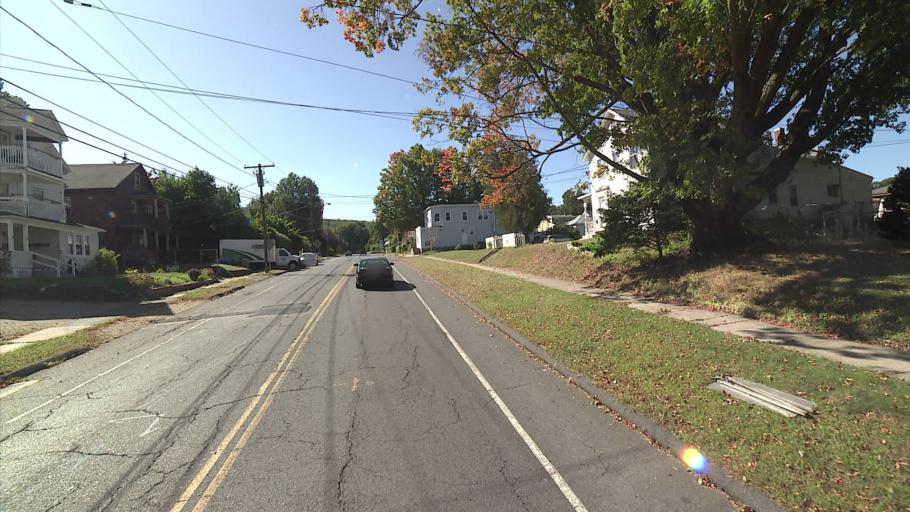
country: US
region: Connecticut
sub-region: Hartford County
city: Bristol
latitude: 41.6658
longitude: -72.9479
